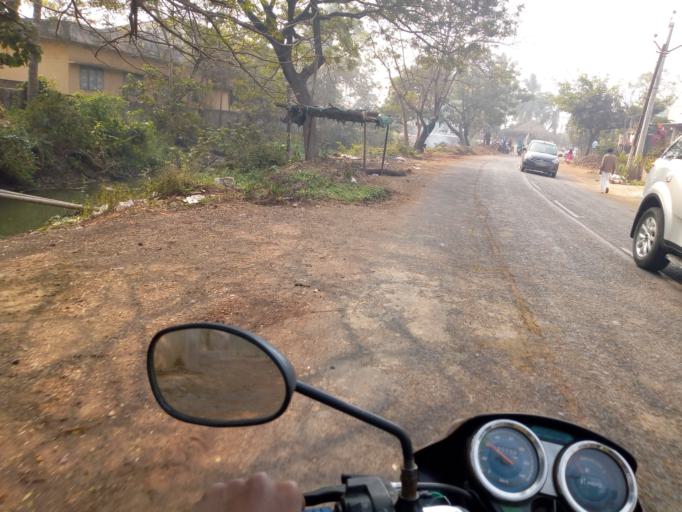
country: IN
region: Andhra Pradesh
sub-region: West Godavari
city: Tadepallegudem
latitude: 16.7774
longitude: 81.4218
